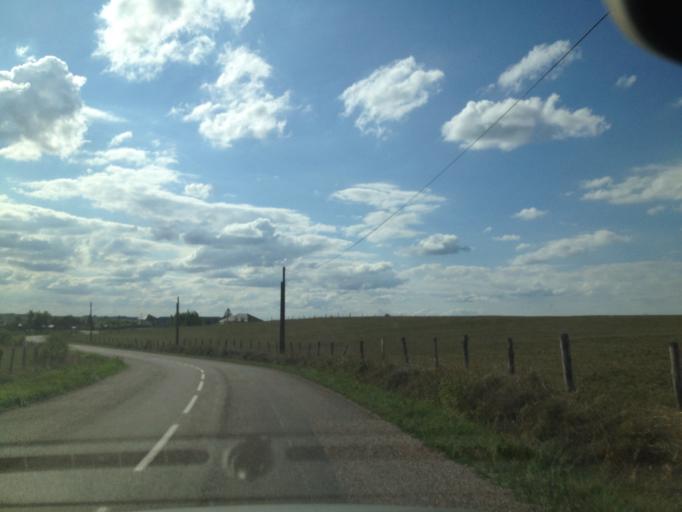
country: FR
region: Franche-Comte
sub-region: Departement de la Haute-Saone
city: Faverney
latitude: 47.8120
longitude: 6.1407
